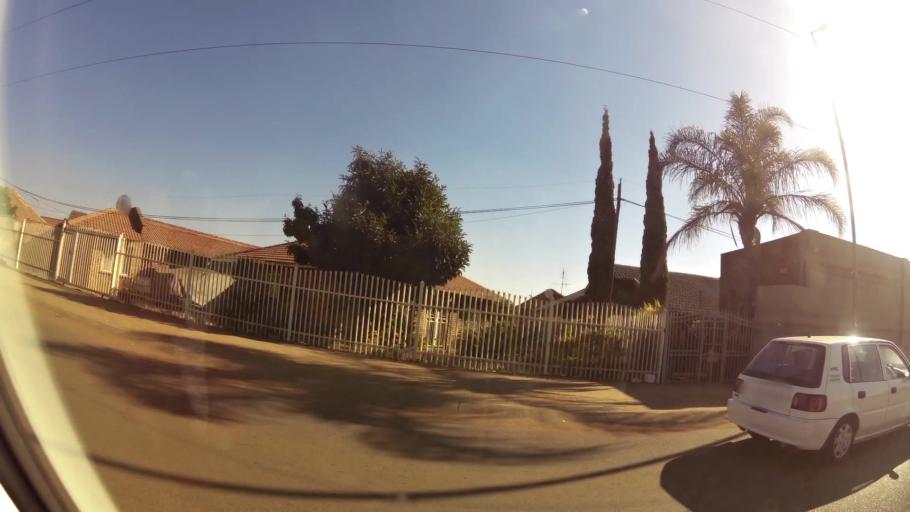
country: ZA
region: Gauteng
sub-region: City of Tshwane Metropolitan Municipality
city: Cullinan
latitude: -25.7158
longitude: 28.3755
